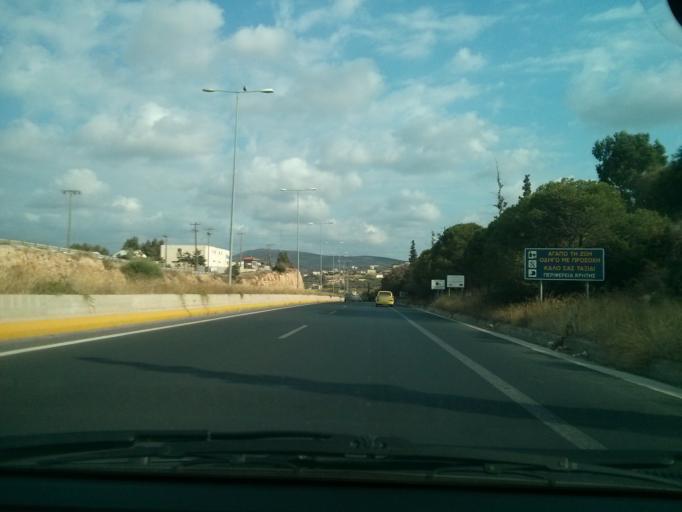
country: GR
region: Crete
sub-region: Nomos Irakleiou
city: Nea Alikarnassos
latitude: 35.3255
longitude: 25.1797
